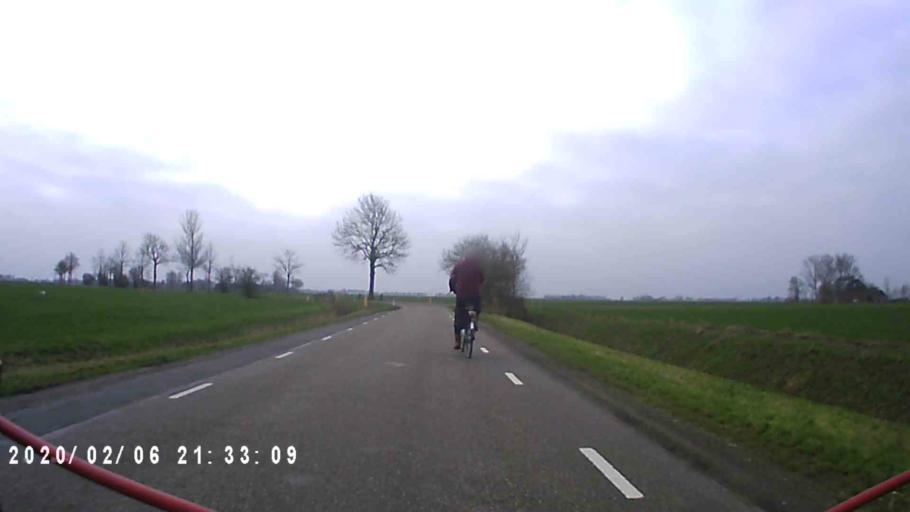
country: NL
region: Groningen
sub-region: Gemeente Zuidhorn
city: Noordhorn
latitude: 53.2776
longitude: 6.3905
